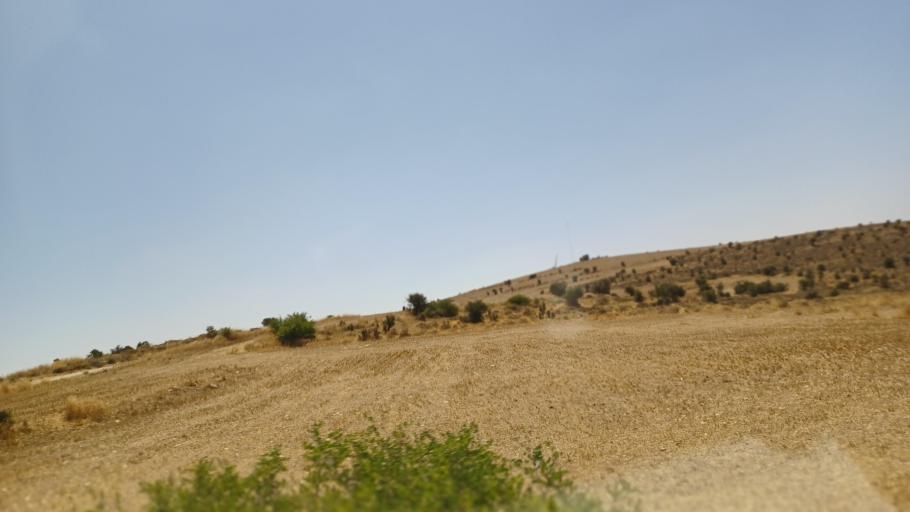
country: CY
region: Larnaka
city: Psevdas
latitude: 34.9716
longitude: 33.4793
